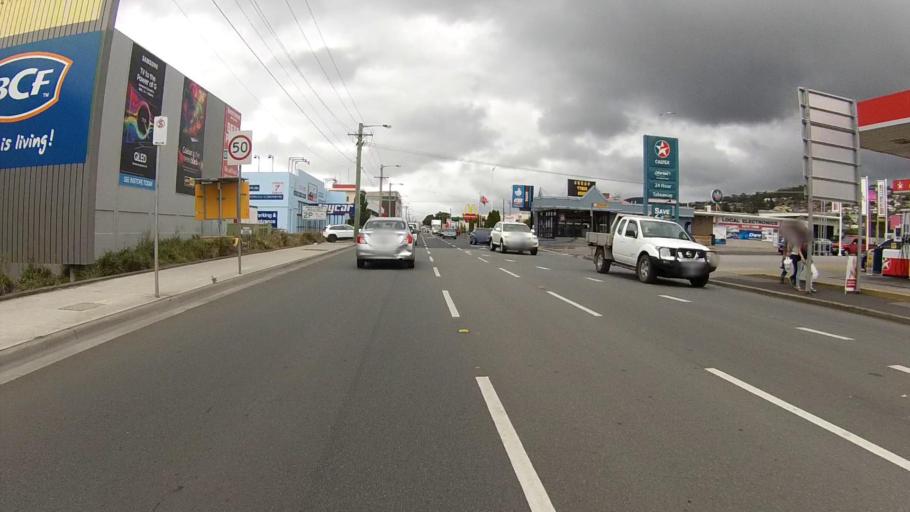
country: AU
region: Tasmania
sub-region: Glenorchy
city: Goodwood
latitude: -42.8406
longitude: 147.2906
